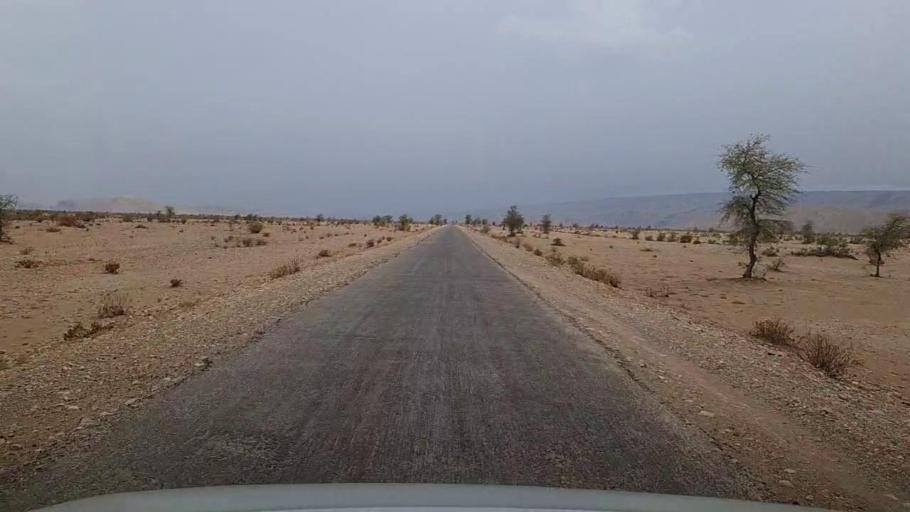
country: PK
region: Sindh
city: Sehwan
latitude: 26.2664
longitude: 67.7235
